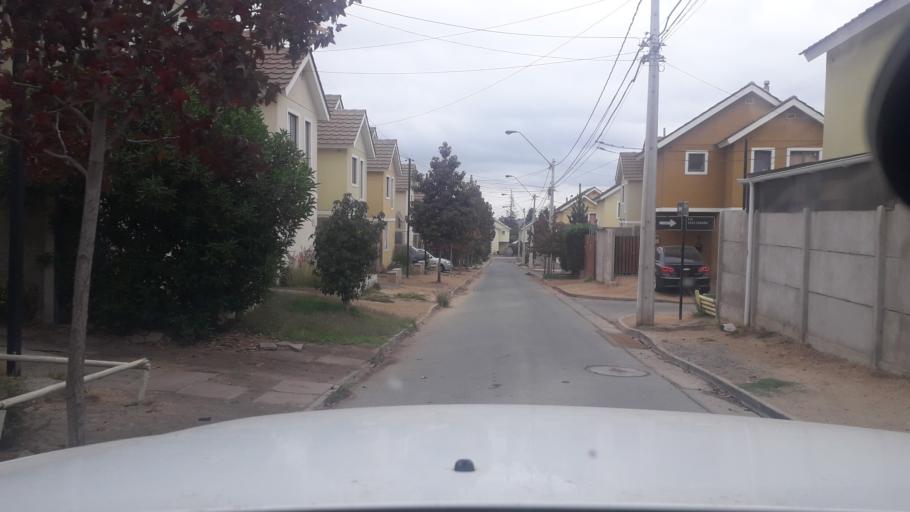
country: CL
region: Valparaiso
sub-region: Provincia de Marga Marga
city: Villa Alemana
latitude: -33.0518
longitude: -71.3352
